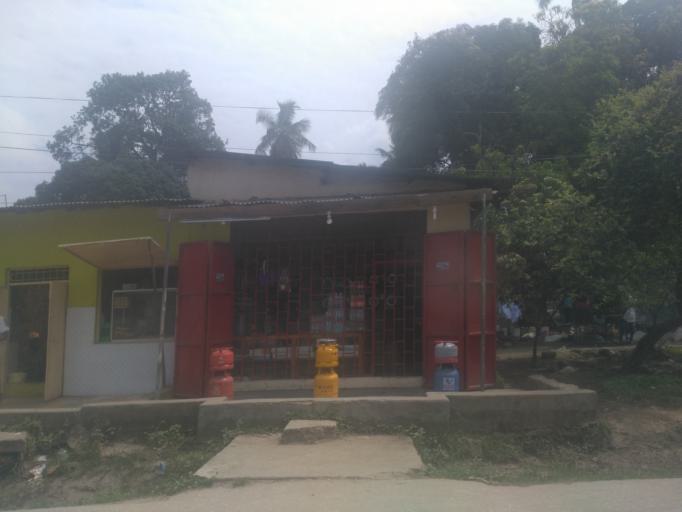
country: TZ
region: Zanzibar Urban/West
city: Zanzibar
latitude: -6.2099
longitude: 39.2168
